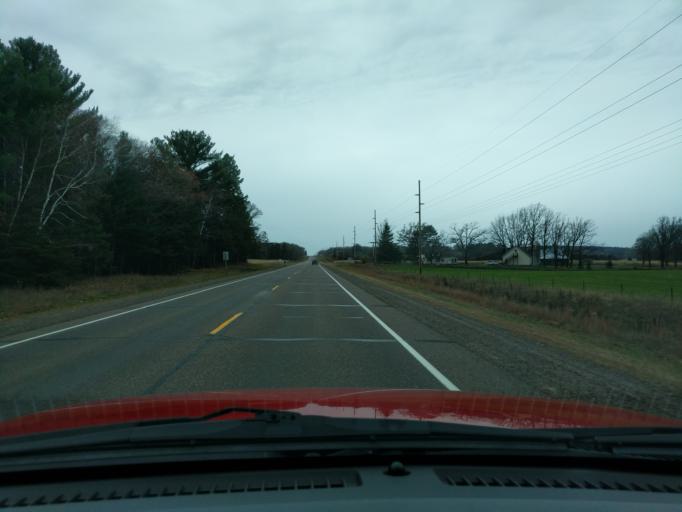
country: US
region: Wisconsin
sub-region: Washburn County
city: Shell Lake
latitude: 45.8151
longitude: -92.0100
